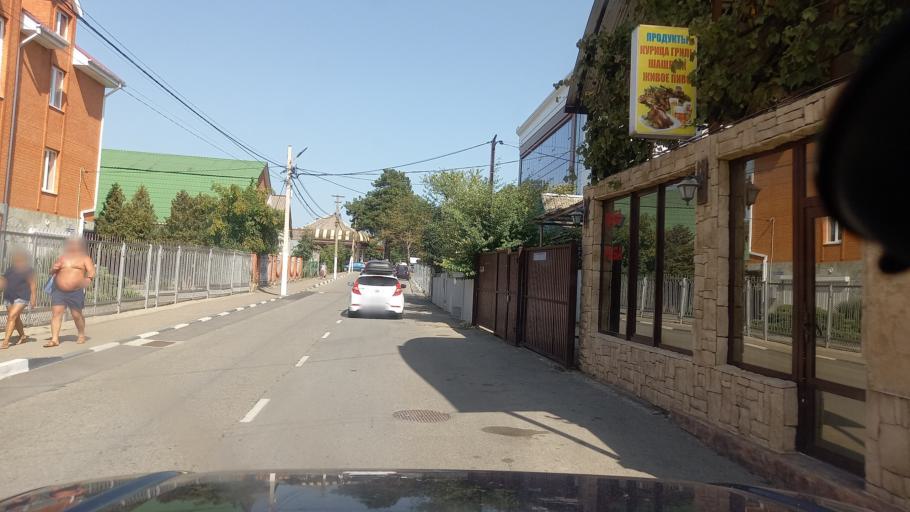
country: RU
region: Krasnodarskiy
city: Arkhipo-Osipovka
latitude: 44.3692
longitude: 38.5326
